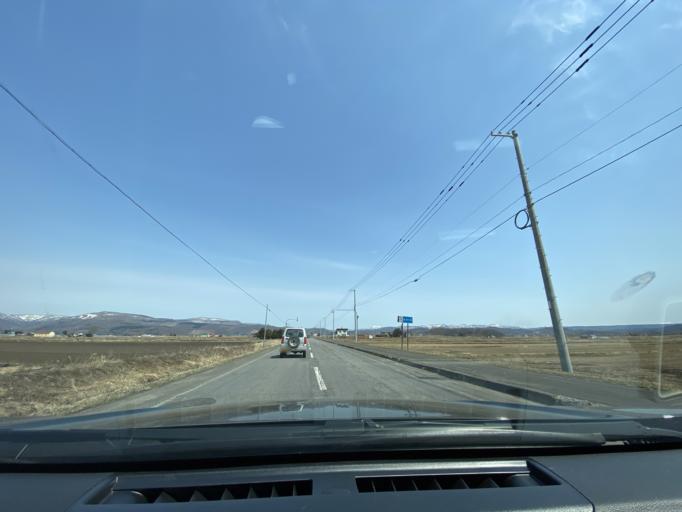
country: JP
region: Hokkaido
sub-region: Asahikawa-shi
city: Asahikawa
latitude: 43.8766
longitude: 142.4957
